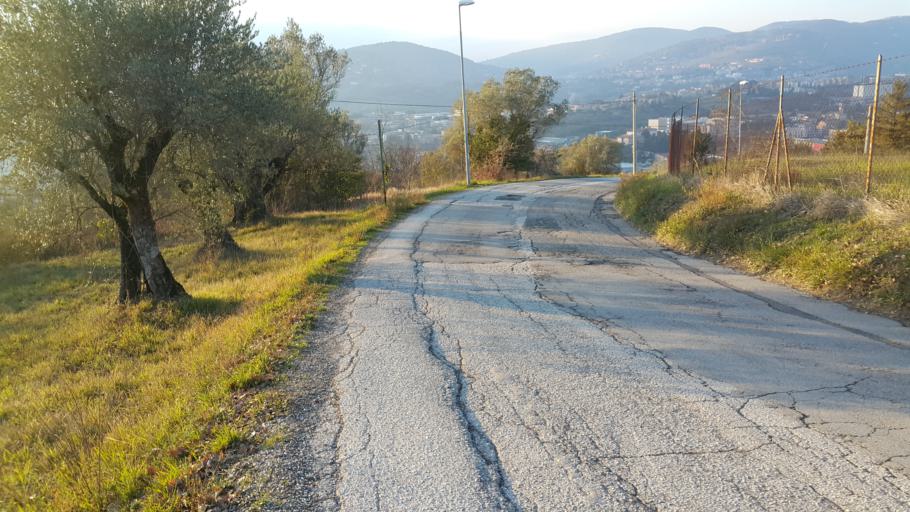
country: IT
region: Umbria
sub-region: Provincia di Perugia
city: Perugia
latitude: 43.0890
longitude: 12.3767
